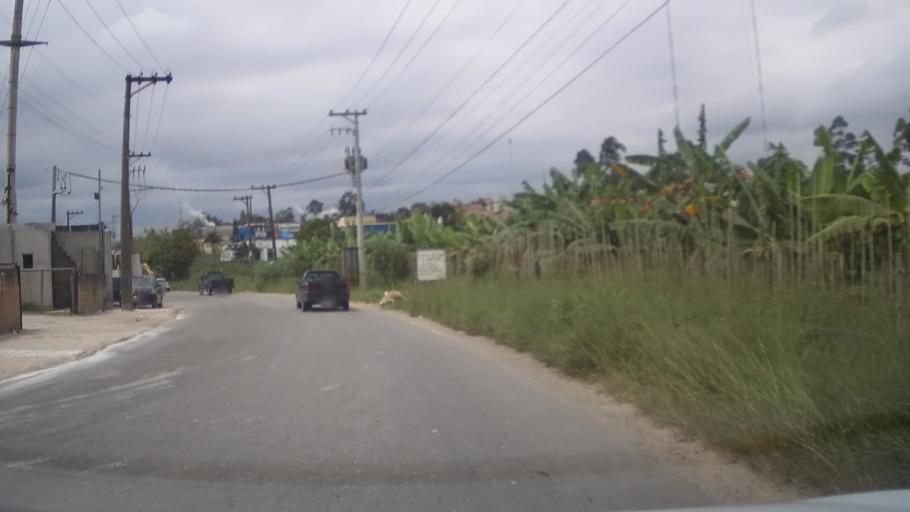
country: BR
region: Sao Paulo
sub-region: Itaquaquecetuba
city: Itaquaquecetuba
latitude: -23.4448
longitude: -46.3923
